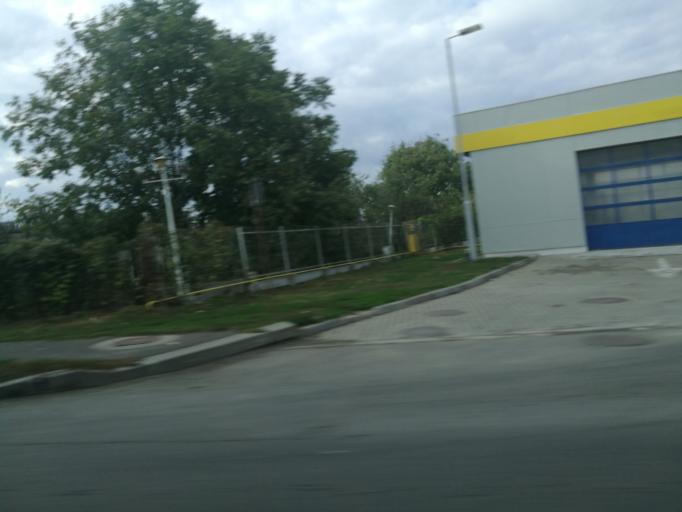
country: RO
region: Mures
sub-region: Comuna Sancraiu de Mures
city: Nazna
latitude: 46.5147
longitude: 24.5167
